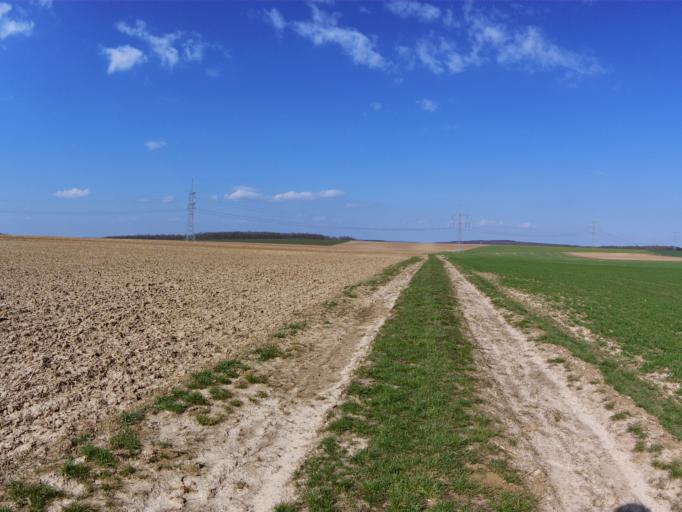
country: DE
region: Bavaria
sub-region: Regierungsbezirk Unterfranken
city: Biebelried
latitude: 49.7935
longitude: 10.0664
